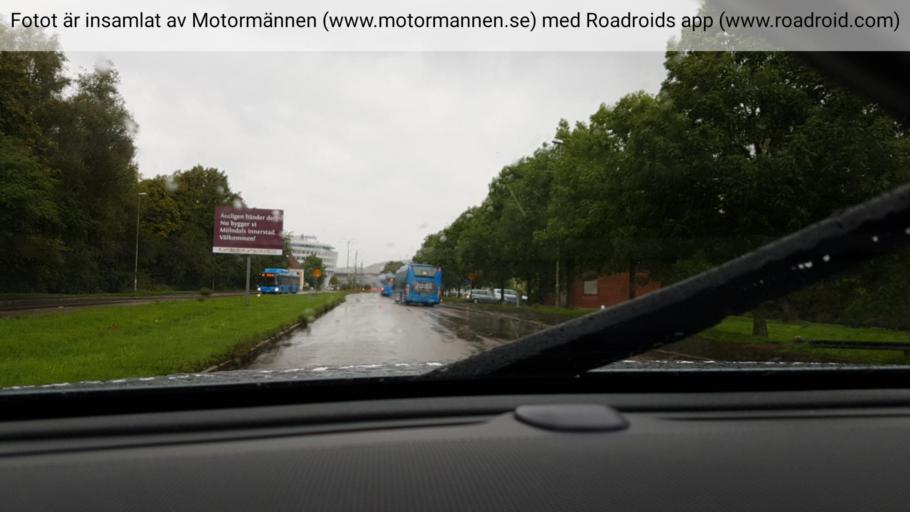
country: SE
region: Vaestra Goetaland
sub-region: Molndal
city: Moelndal
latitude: 57.6503
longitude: 12.0184
